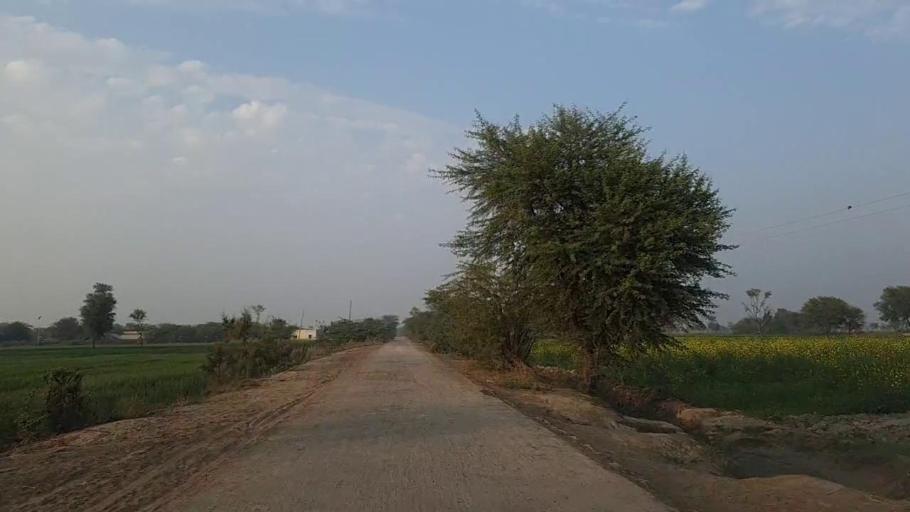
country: PK
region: Sindh
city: Jam Sahib
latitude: 26.3136
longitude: 68.6090
